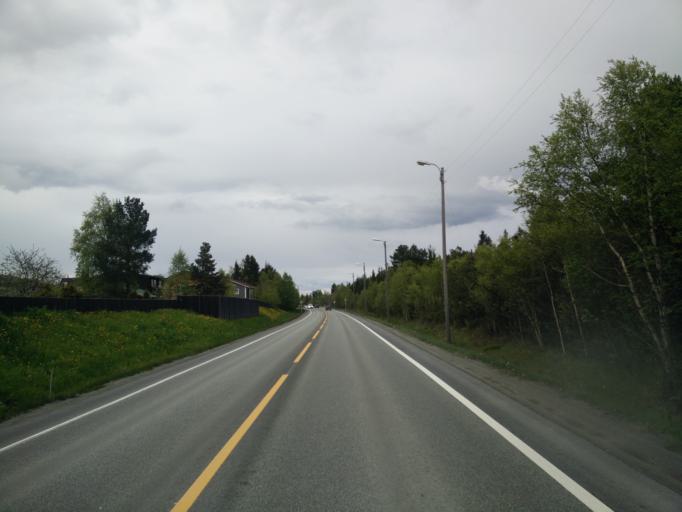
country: NO
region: Sor-Trondelag
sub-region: Trondheim
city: Trondheim
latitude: 63.3447
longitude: 10.3678
